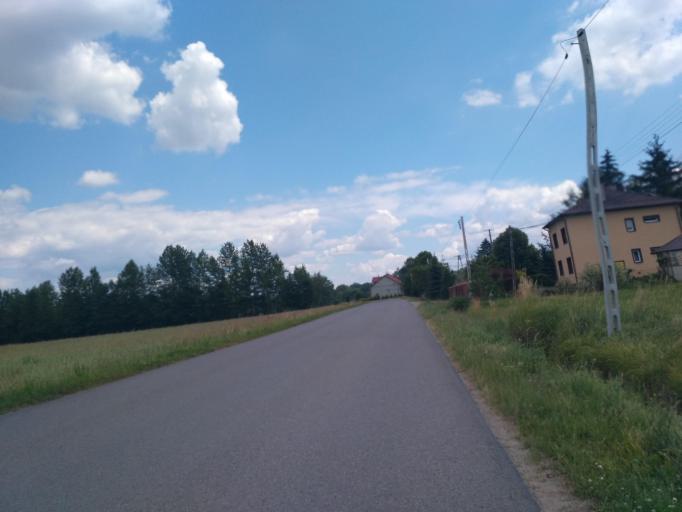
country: PL
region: Subcarpathian Voivodeship
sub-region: Powiat debicki
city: Brzostek
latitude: 49.8593
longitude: 21.4333
